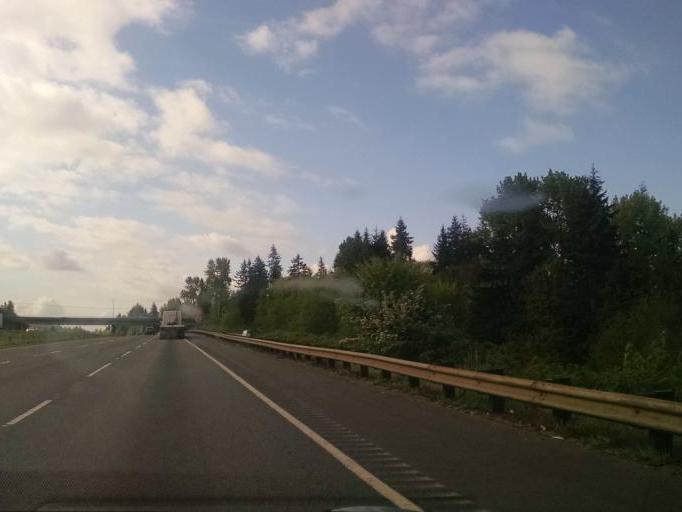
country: US
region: Washington
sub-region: Cowlitz County
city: Kelso
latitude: 46.1553
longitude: -122.9020
